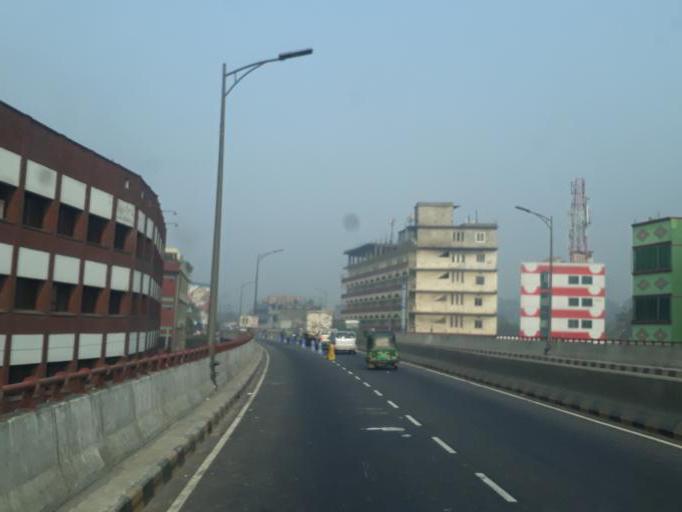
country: BD
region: Dhaka
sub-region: Dhaka
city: Dhaka
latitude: 23.7207
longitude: 90.4178
